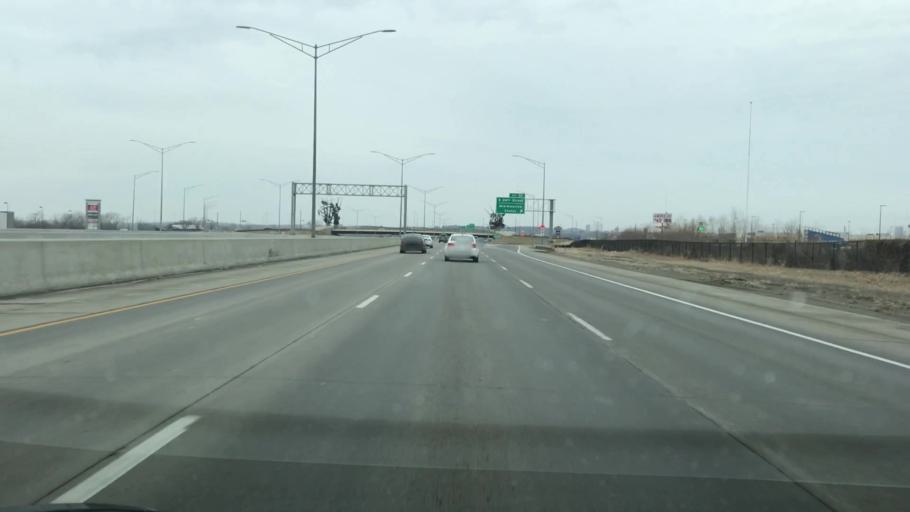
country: US
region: Iowa
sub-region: Pottawattamie County
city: Council Bluffs
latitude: 41.2328
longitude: -95.8726
